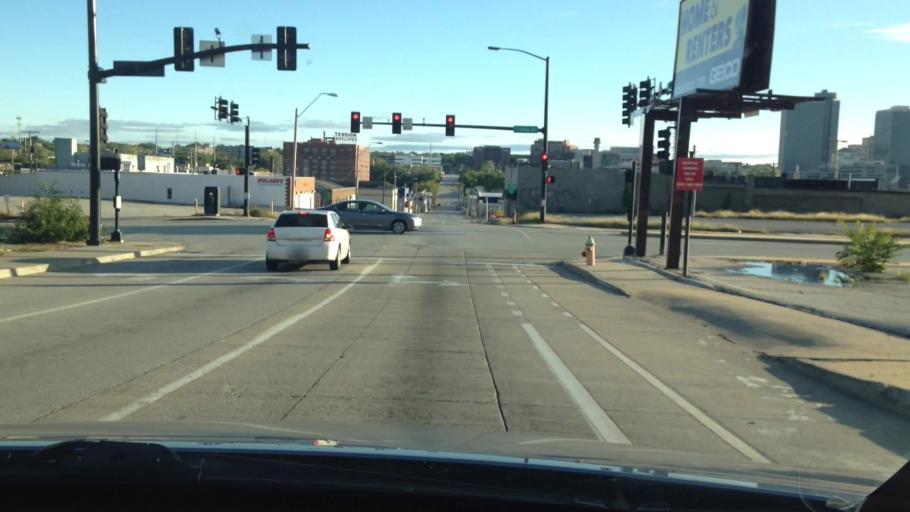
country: US
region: Missouri
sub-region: Jackson County
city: Kansas City
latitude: 39.0960
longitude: -94.5742
